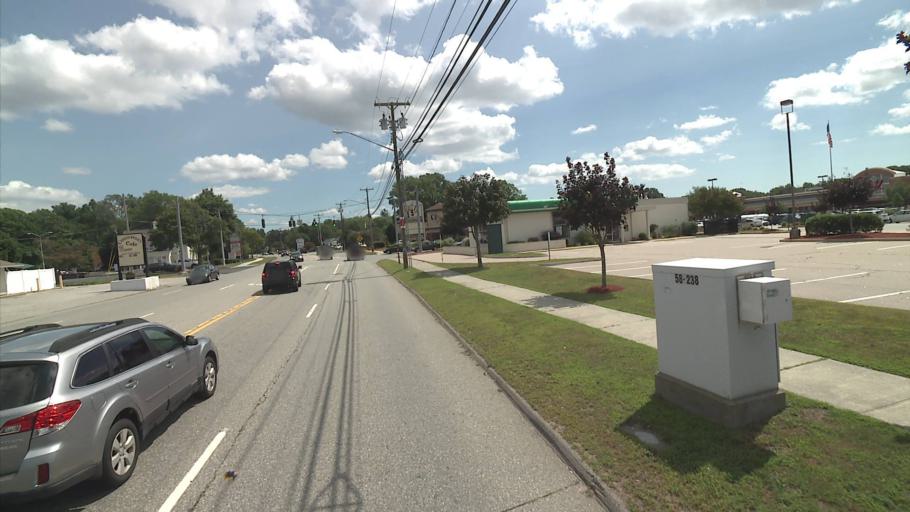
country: US
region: Connecticut
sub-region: New London County
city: Long Hill
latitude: 41.3464
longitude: -72.0500
